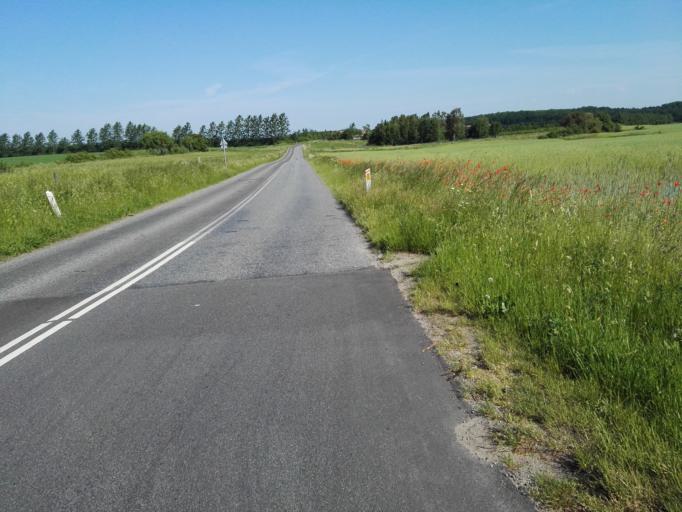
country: DK
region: Zealand
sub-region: Lejre Kommune
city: Ejby
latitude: 55.7196
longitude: 11.8904
